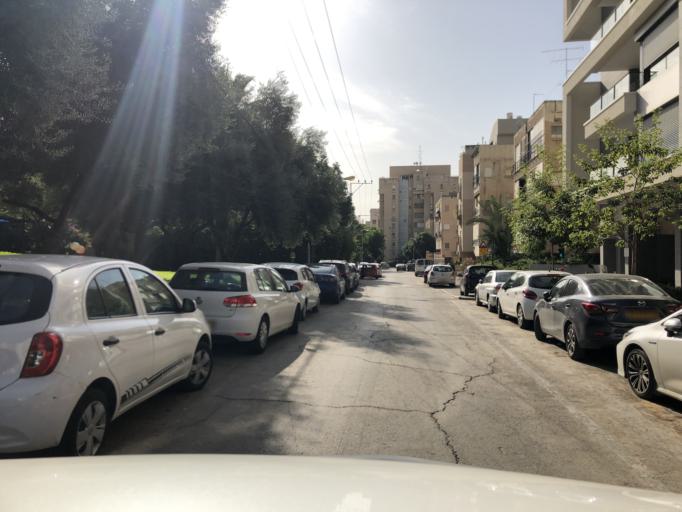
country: IL
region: Tel Aviv
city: Bene Beraq
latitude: 32.0687
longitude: 34.8307
